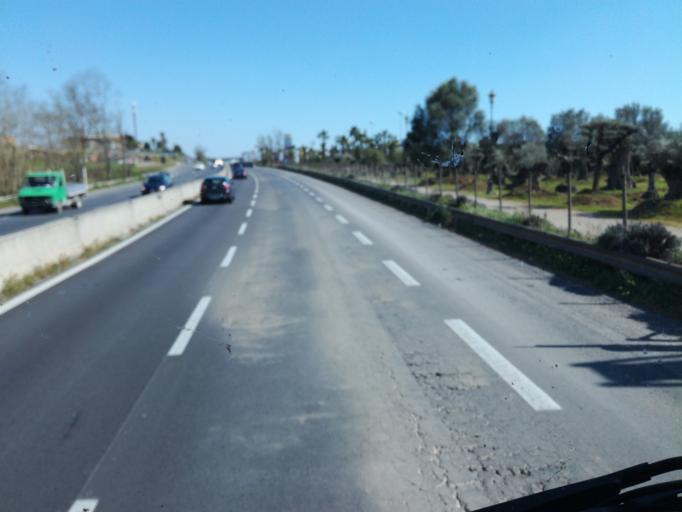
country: IT
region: Latium
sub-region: Provincia di Latina
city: Camilleri-Vallelata
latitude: 41.5959
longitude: 12.6253
